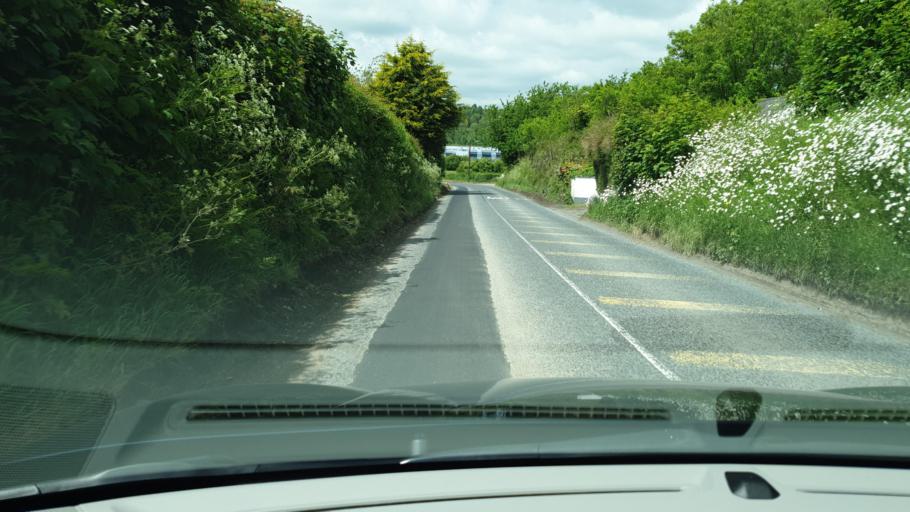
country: IE
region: Ulster
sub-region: An Cabhan
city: Kingscourt
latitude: 53.9025
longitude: -6.7816
